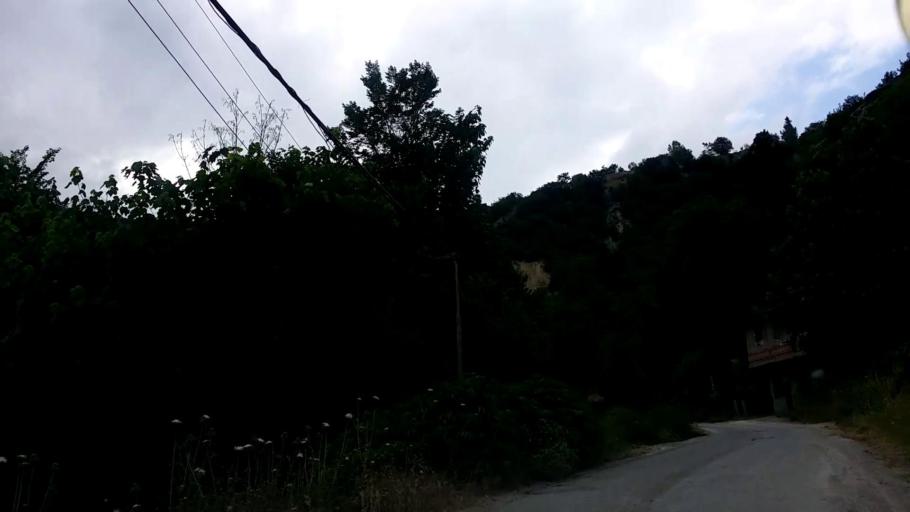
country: IR
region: Mazandaran
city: Chalus
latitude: 36.5551
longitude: 51.2760
